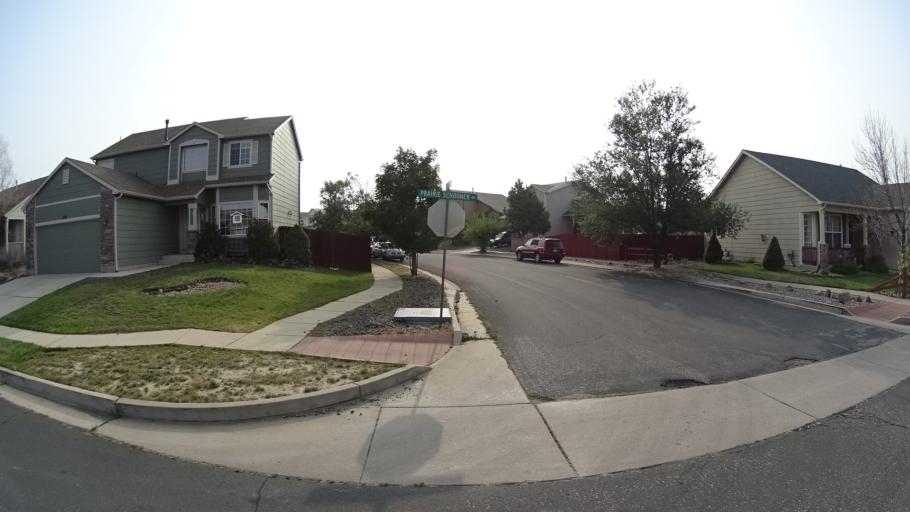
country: US
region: Colorado
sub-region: El Paso County
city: Cimarron Hills
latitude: 38.9335
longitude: -104.7275
